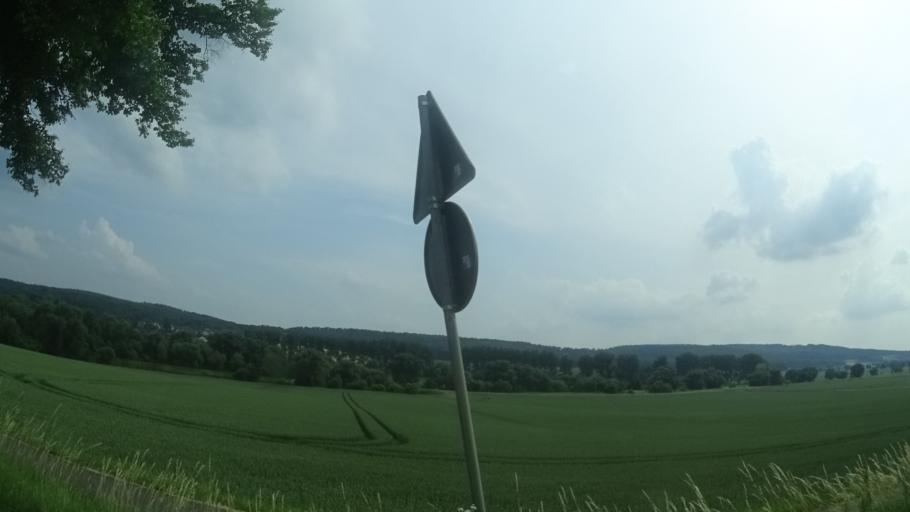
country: DE
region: Lower Saxony
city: Holle
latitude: 52.1055
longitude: 10.1191
